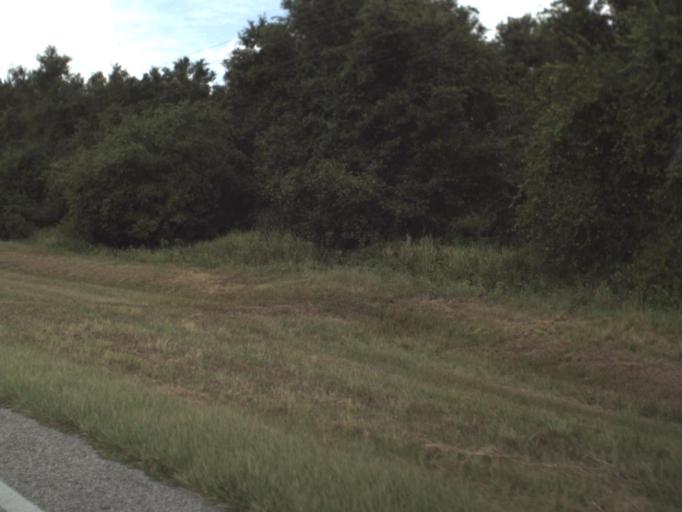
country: US
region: Florida
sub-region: Hardee County
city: Bowling Green
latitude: 27.6814
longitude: -81.8180
